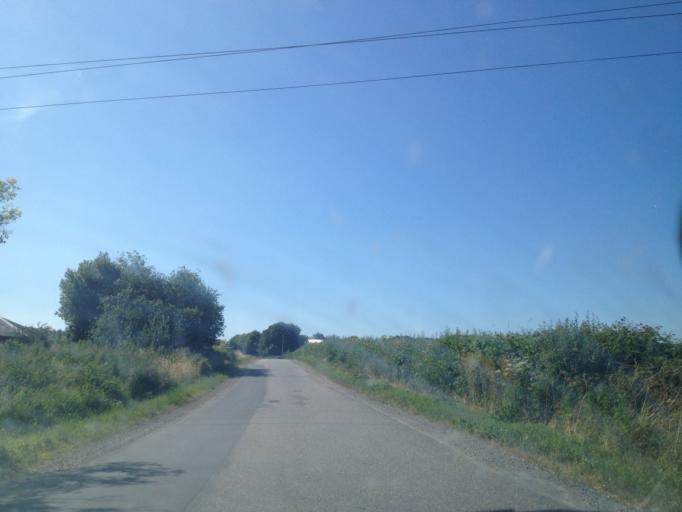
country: DK
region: South Denmark
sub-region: Kolding Kommune
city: Christiansfeld
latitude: 55.4063
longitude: 9.5067
